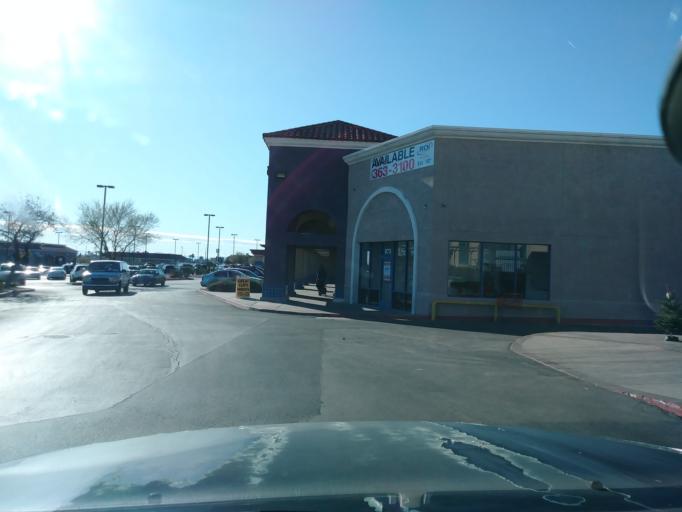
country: US
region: Nevada
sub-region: Clark County
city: Spring Valley
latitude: 36.1621
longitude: -115.2453
